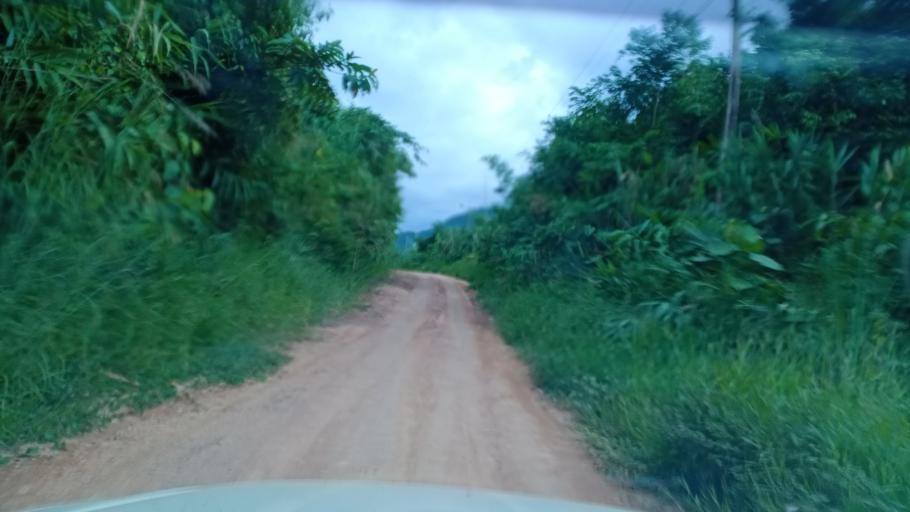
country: TH
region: Changwat Bueng Kan
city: Pak Khat
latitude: 18.7271
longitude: 103.2762
